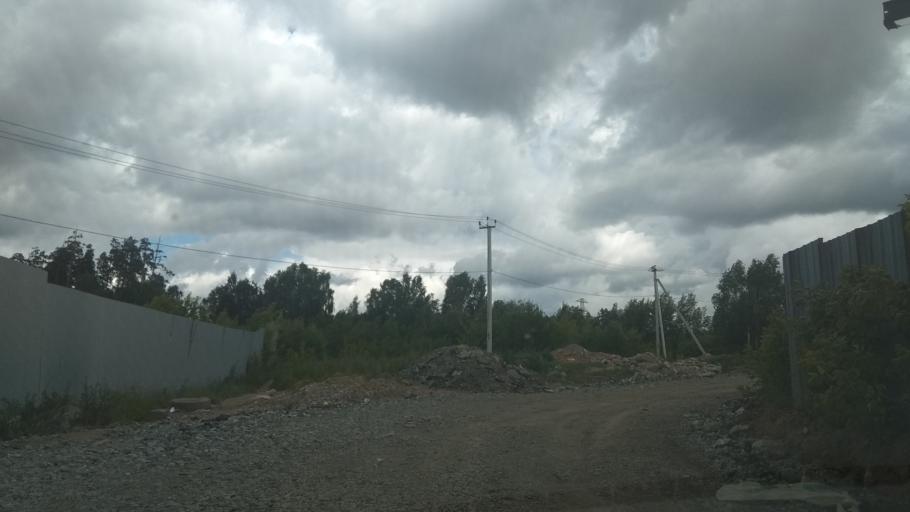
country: RU
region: Sverdlovsk
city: Verkhnyaya Pyshma
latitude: 56.9187
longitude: 60.5708
